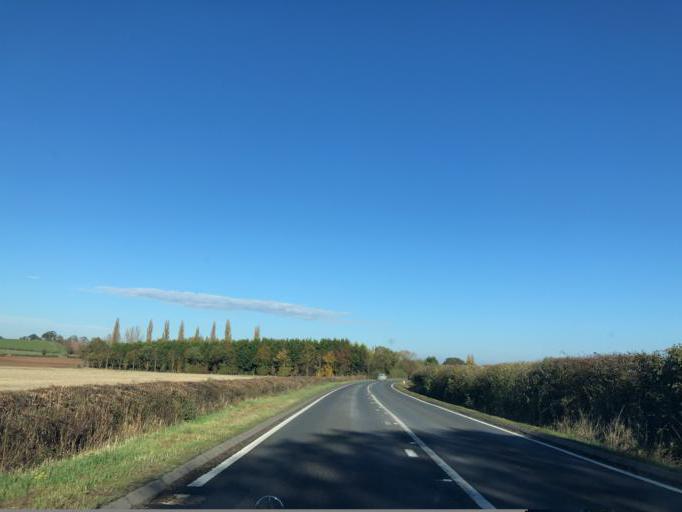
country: GB
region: England
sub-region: Warwickshire
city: Harbury
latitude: 52.2512
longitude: -1.4877
